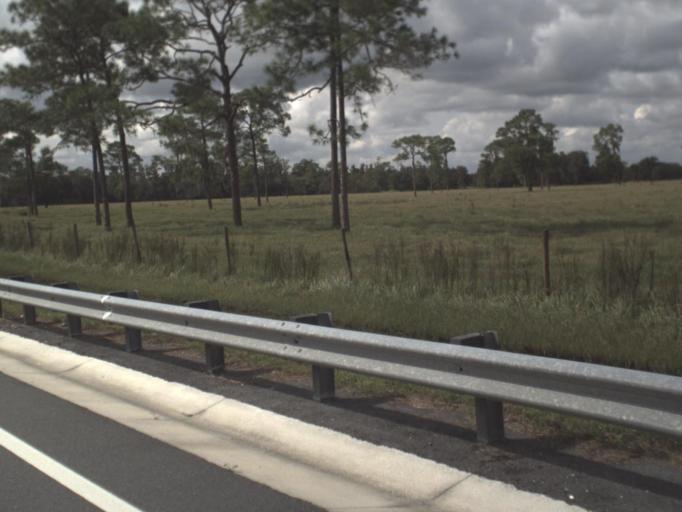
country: US
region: Florida
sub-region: DeSoto County
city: Nocatee
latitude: 27.1999
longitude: -81.9905
